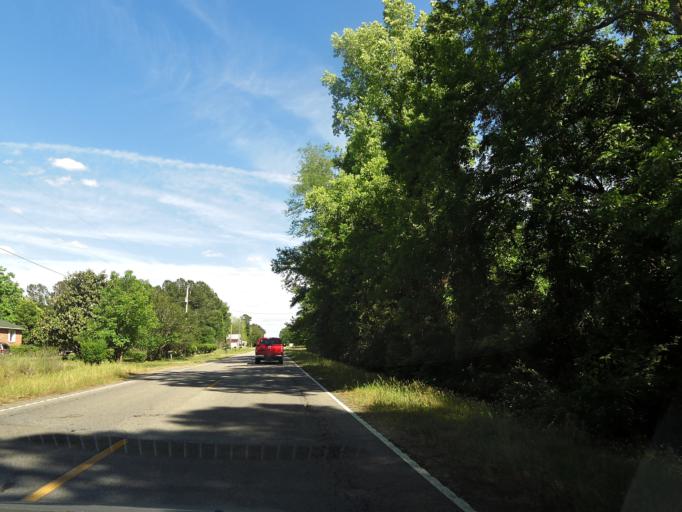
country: US
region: South Carolina
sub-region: Bamberg County
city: Denmark
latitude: 33.3377
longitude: -81.1698
